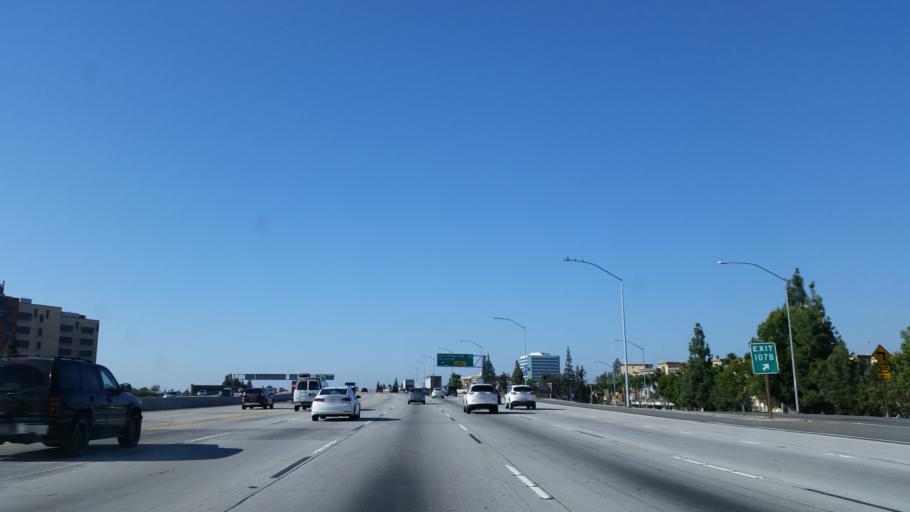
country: US
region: California
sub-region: Orange County
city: Orange
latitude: 33.7871
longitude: -117.8851
